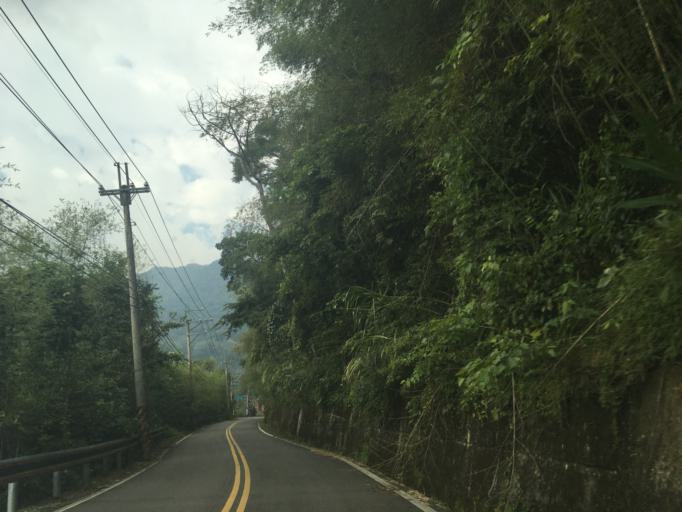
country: TW
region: Taiwan
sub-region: Miaoli
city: Miaoli
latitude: 24.3530
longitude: 120.9460
